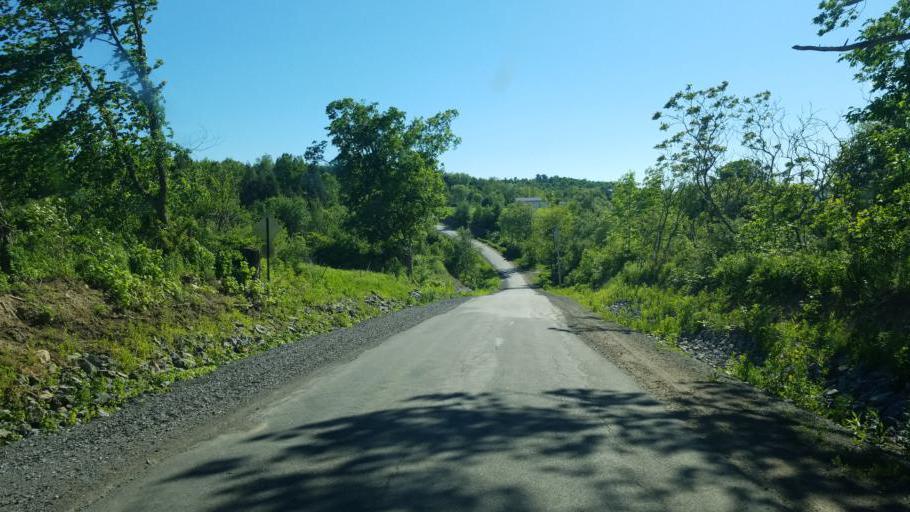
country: US
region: New York
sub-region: Montgomery County
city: Saint Johnsville
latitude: 42.9805
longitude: -74.7742
